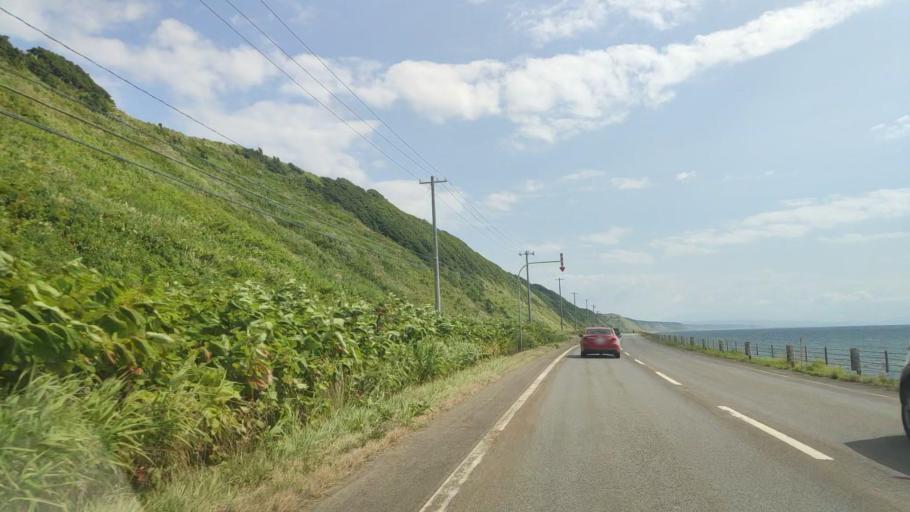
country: JP
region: Hokkaido
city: Rumoi
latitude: 44.0903
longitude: 141.6611
